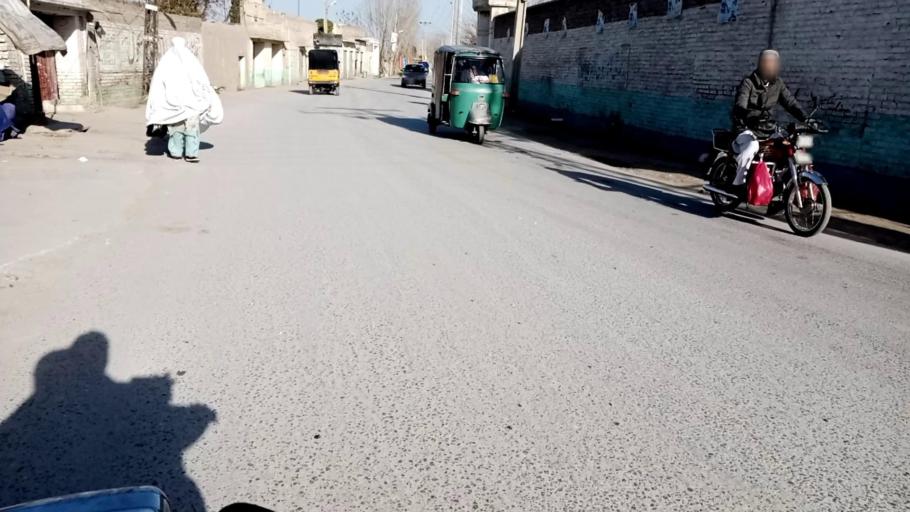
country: PK
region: Khyber Pakhtunkhwa
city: Peshawar
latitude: 34.0550
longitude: 71.5347
